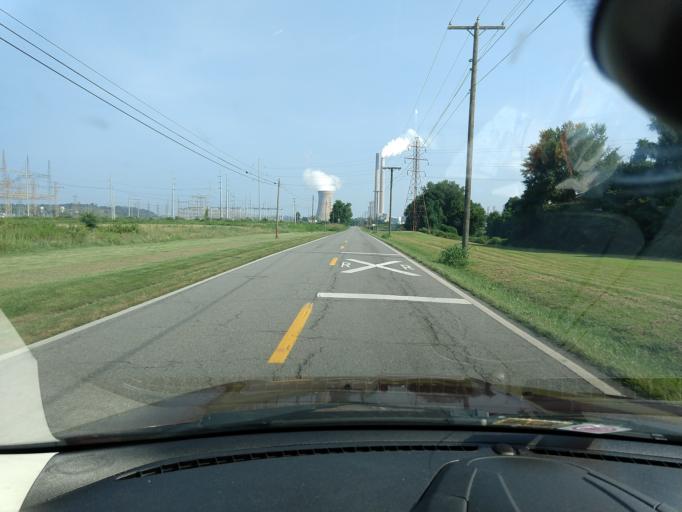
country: US
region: West Virginia
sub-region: Mason County
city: New Haven
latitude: 38.9599
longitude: -81.9250
